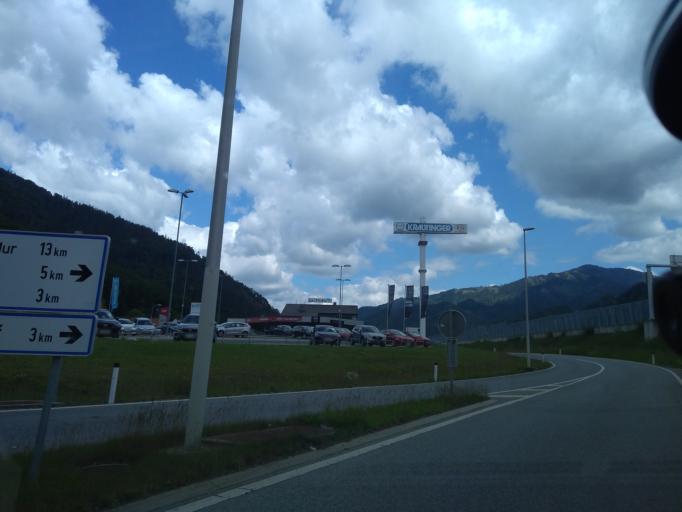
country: AT
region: Styria
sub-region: Politischer Bezirk Bruck-Muerzzuschlag
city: Pernegg an der Mur
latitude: 47.3426
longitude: 15.3486
